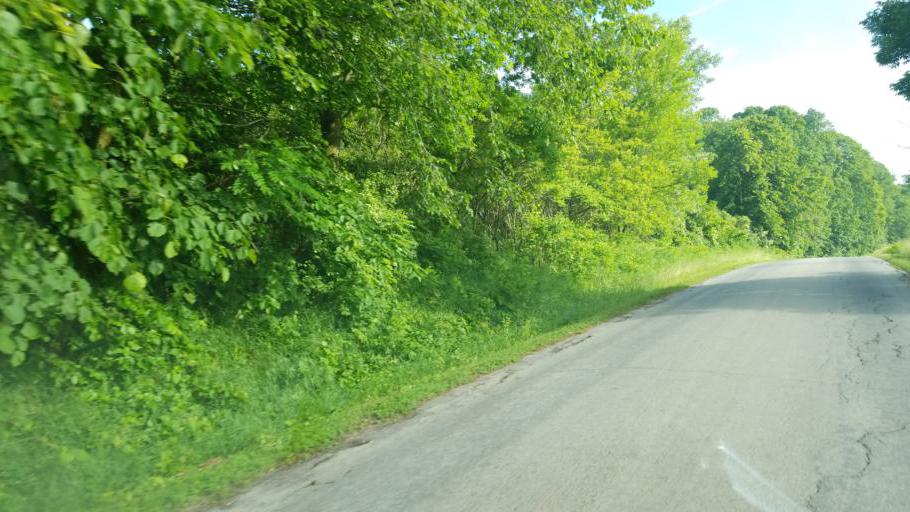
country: US
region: Wisconsin
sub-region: Vernon County
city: Hillsboro
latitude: 43.6012
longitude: -90.3701
